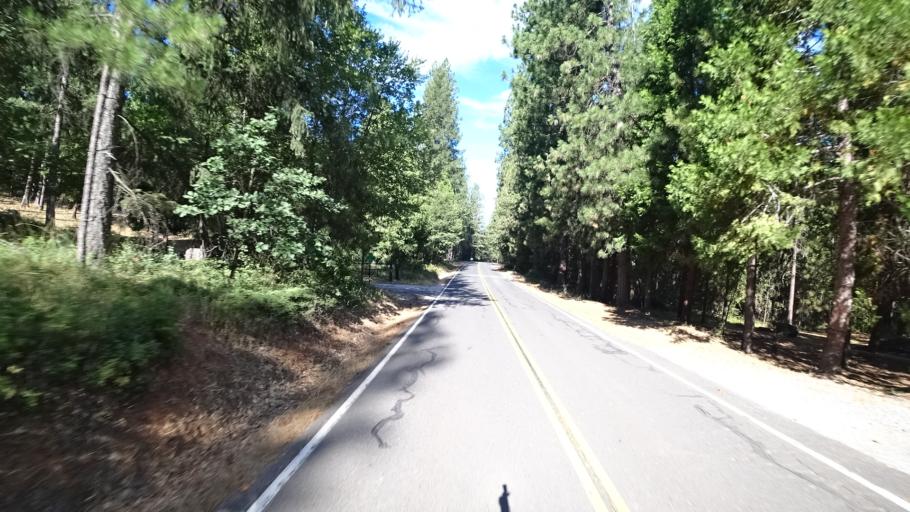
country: US
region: California
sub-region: Amador County
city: Pioneer
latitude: 38.3764
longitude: -120.4867
